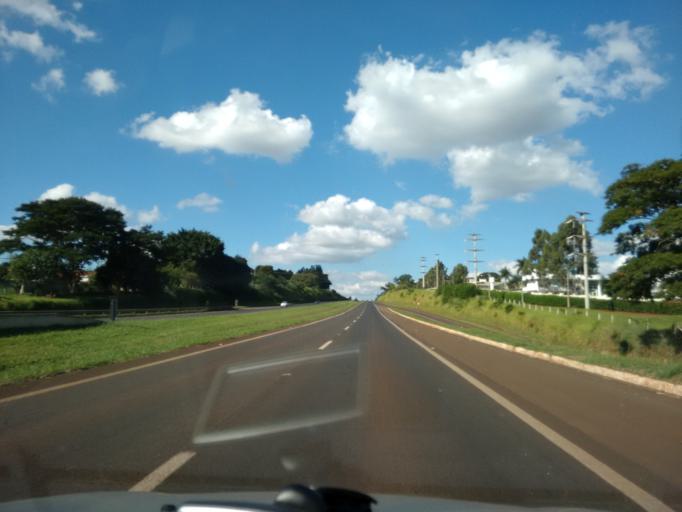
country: BR
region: Sao Paulo
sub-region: Araraquara
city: Araraquara
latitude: -21.8153
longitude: -48.1693
